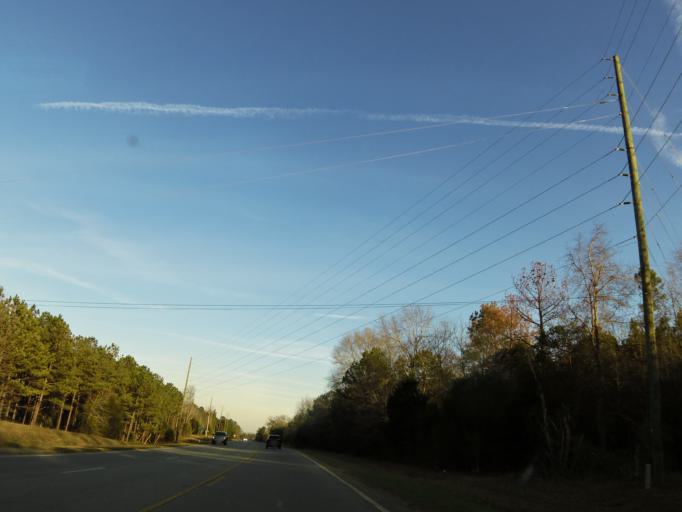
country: US
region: Georgia
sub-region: Sumter County
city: Americus
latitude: 32.0551
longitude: -84.3127
